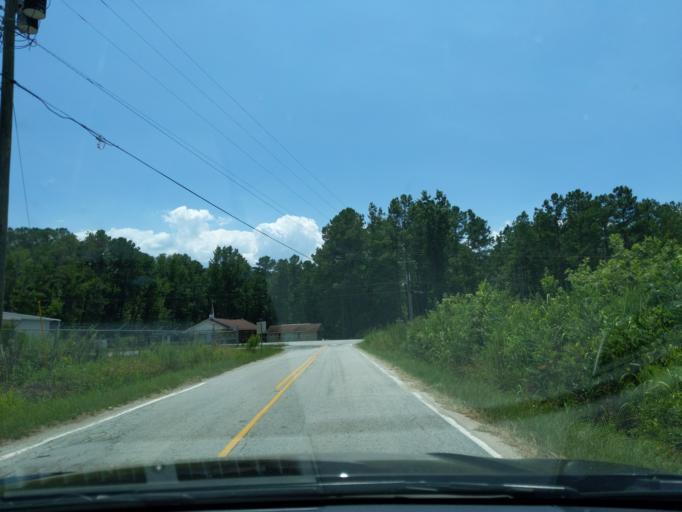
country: US
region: South Carolina
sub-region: Richland County
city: Hopkins
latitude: 33.9068
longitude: -80.9311
